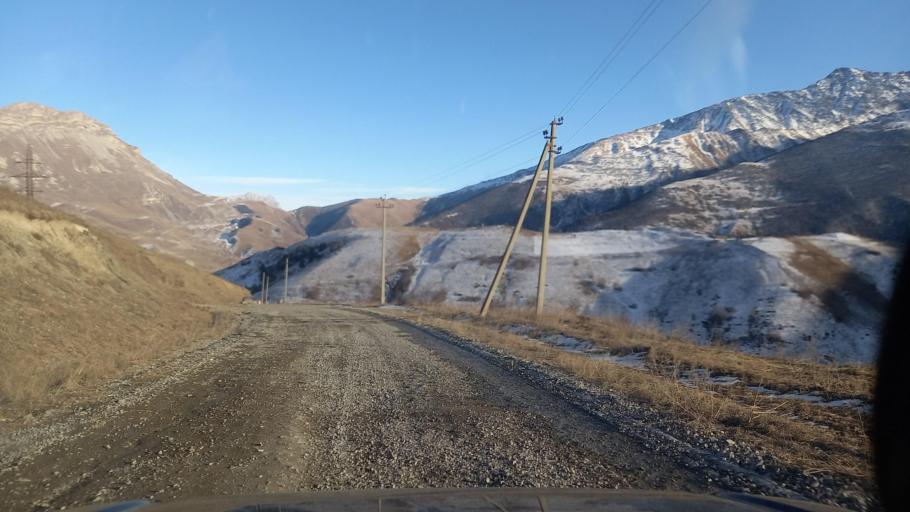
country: RU
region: North Ossetia
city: Verkhniy Fiagdon
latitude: 42.8341
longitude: 44.4849
